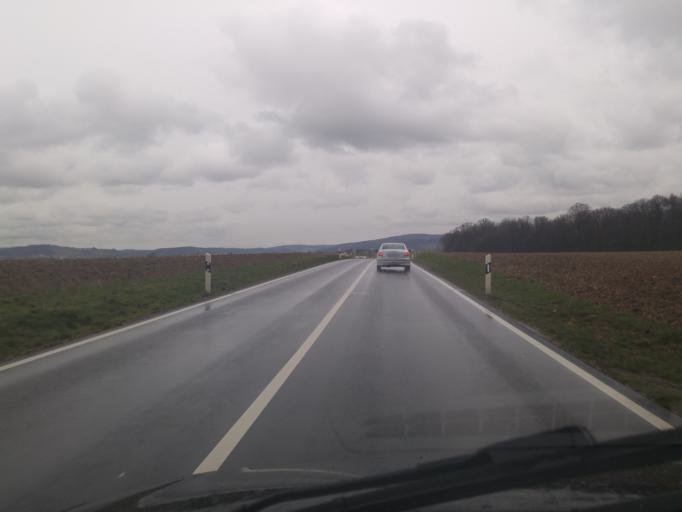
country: DE
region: Baden-Wuerttemberg
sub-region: Regierungsbezirk Stuttgart
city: Affalterbach
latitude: 48.9071
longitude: 9.3429
